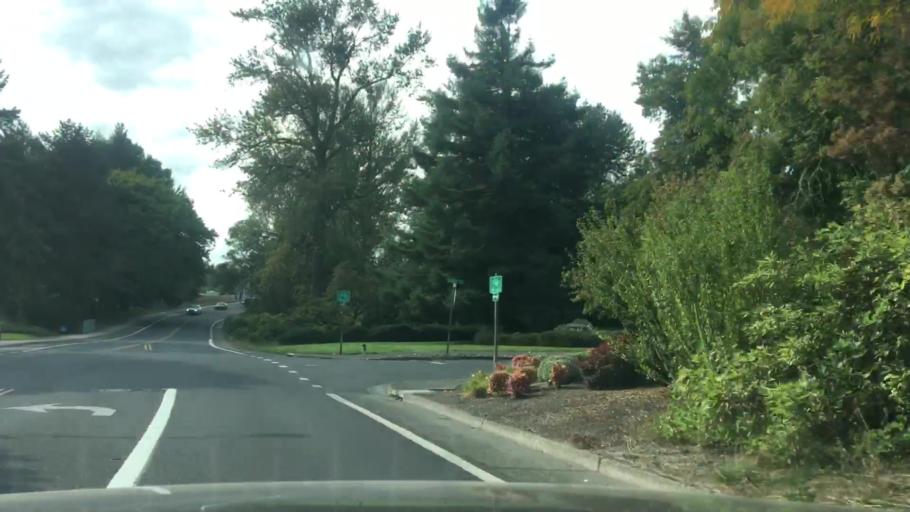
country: US
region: Oregon
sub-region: Lane County
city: Eugene
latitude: 44.0842
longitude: -123.0983
